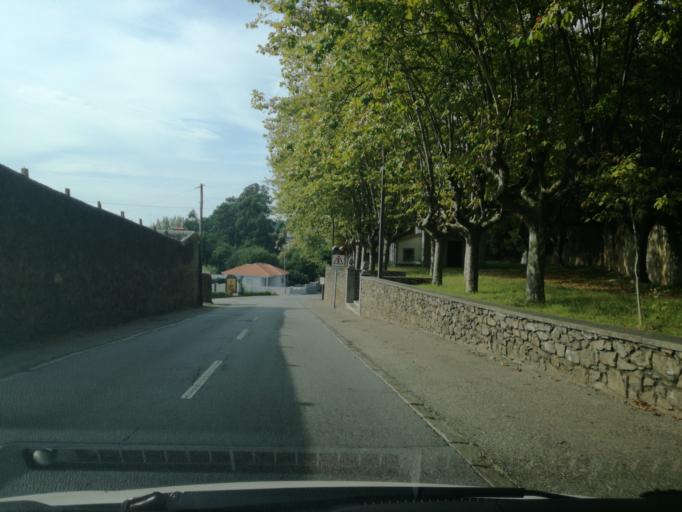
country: PT
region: Porto
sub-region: Vila Nova de Gaia
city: Arcozelo
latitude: 41.0582
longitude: -8.6270
